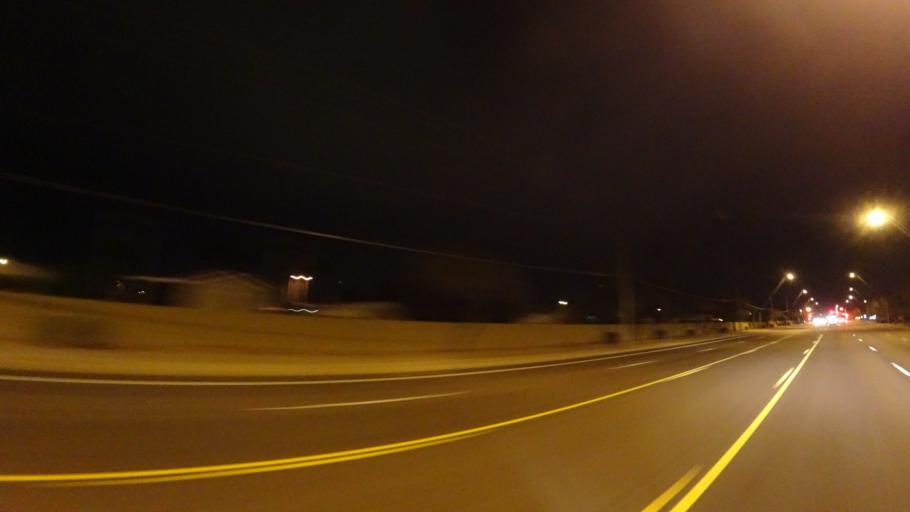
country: US
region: Arizona
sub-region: Maricopa County
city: Gilbert
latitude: 33.4115
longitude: -111.7365
